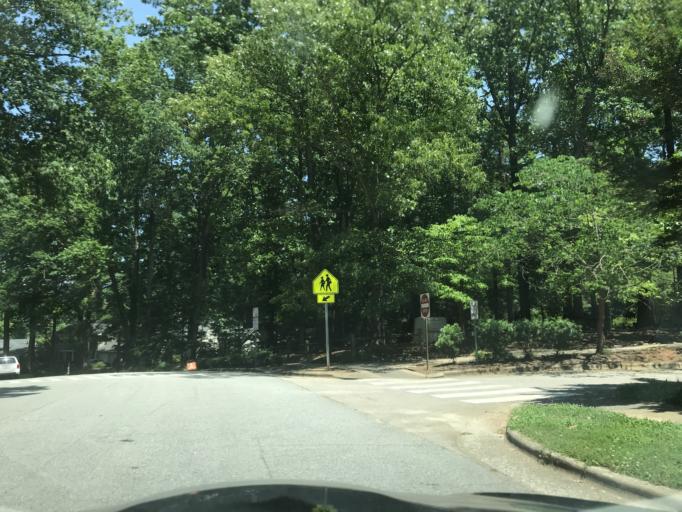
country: US
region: North Carolina
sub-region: Wake County
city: West Raleigh
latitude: 35.8411
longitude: -78.6293
